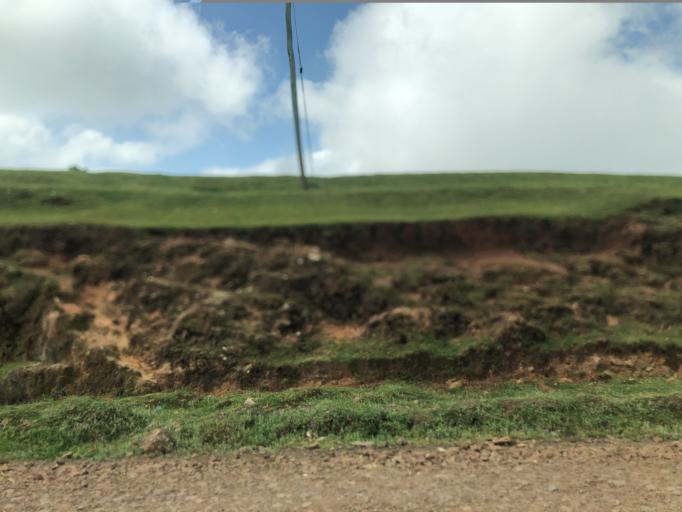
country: ET
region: Southern Nations, Nationalities, and People's Region
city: Arba Minch'
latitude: 6.2030
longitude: 37.5710
